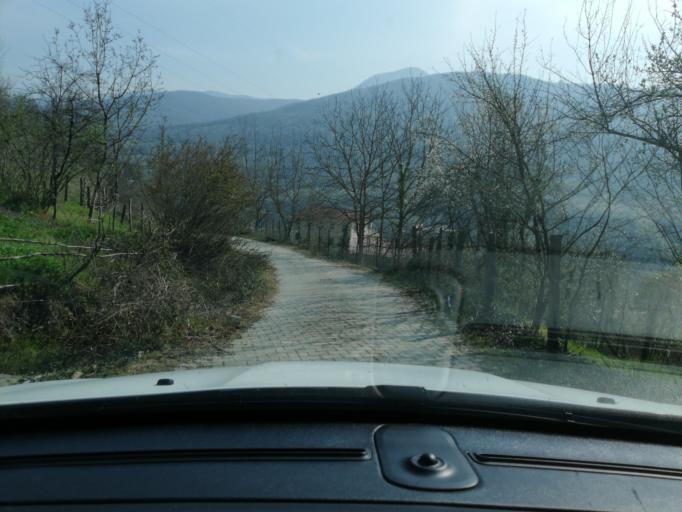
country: TR
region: Karabuk
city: Yenice
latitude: 41.2710
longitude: 32.3592
